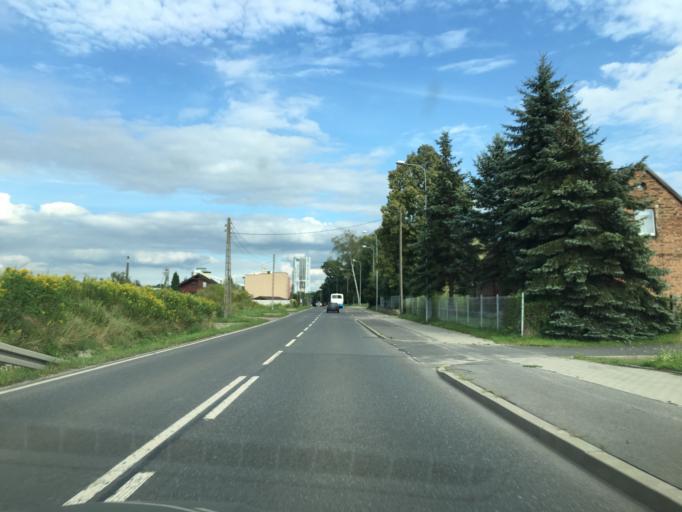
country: PL
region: Silesian Voivodeship
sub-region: Ruda Slaska
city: Ruda Slaska
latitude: 50.2649
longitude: 18.8166
